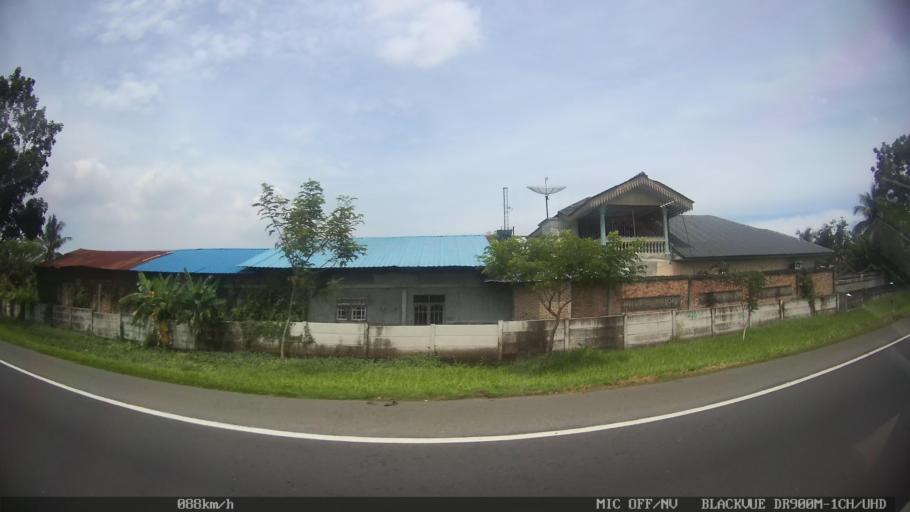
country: ID
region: North Sumatra
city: Labuhan Deli
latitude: 3.7160
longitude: 98.6824
